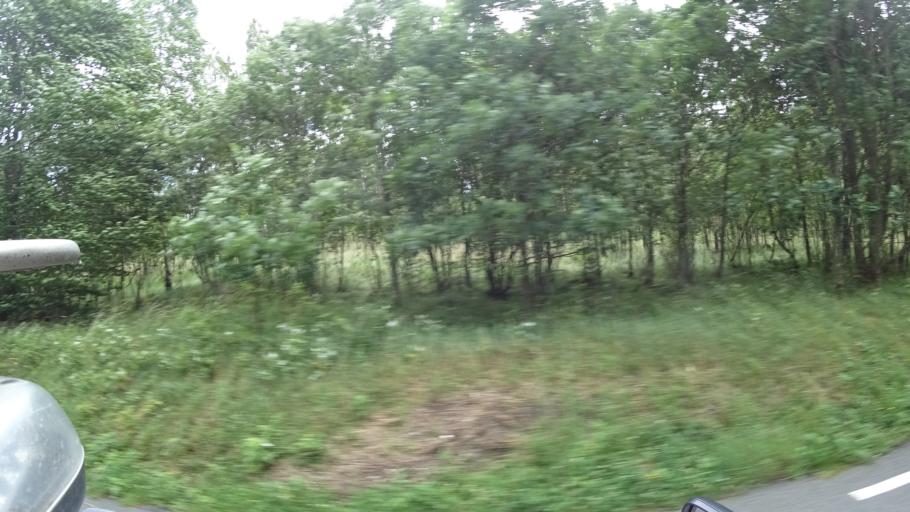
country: SE
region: Skane
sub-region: Kristianstads Kommun
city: Degeberga
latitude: 55.7212
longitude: 13.9935
